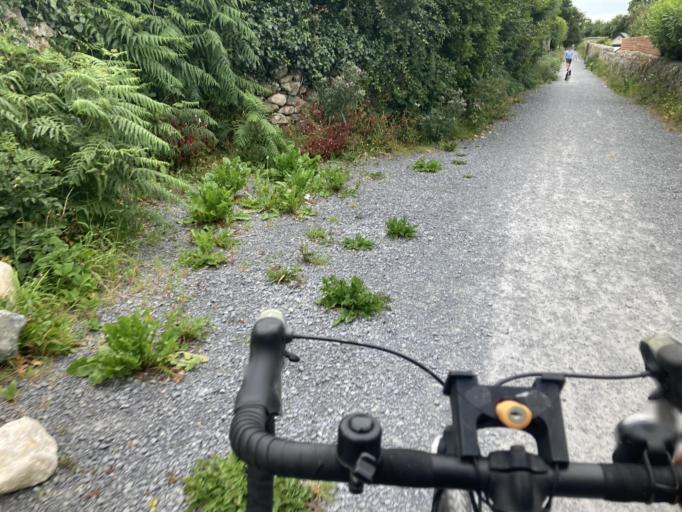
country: IE
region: Connaught
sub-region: County Galway
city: Gaillimh
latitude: 53.2690
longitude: -9.0945
